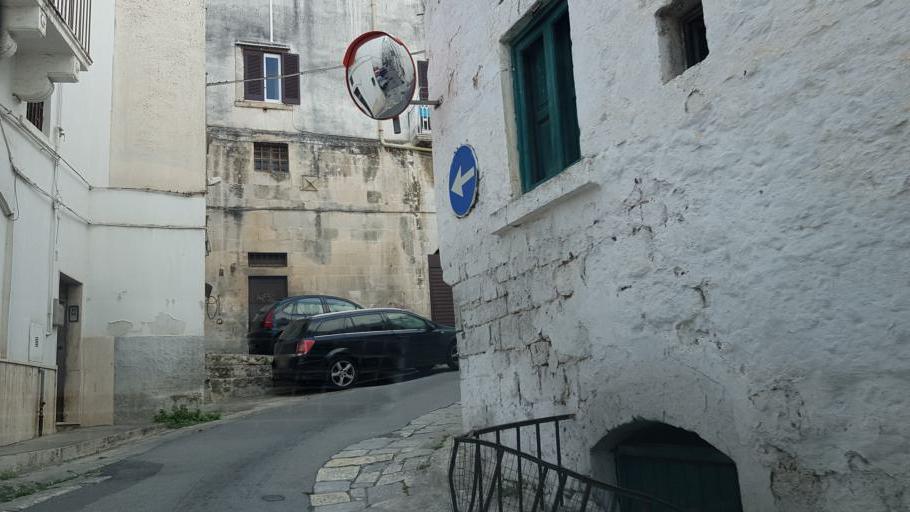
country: IT
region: Apulia
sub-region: Provincia di Brindisi
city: Ostuni
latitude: 40.7313
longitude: 17.5799
